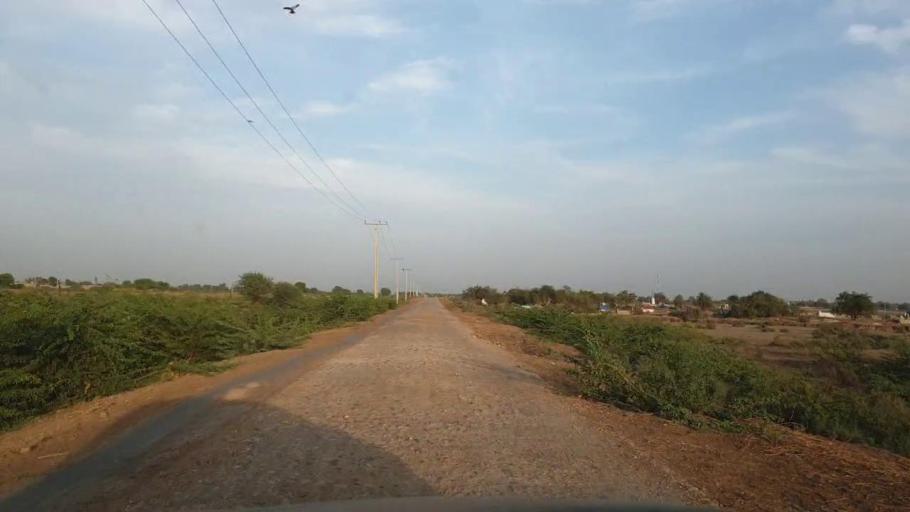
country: PK
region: Sindh
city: Kunri
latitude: 25.1610
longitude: 69.5690
